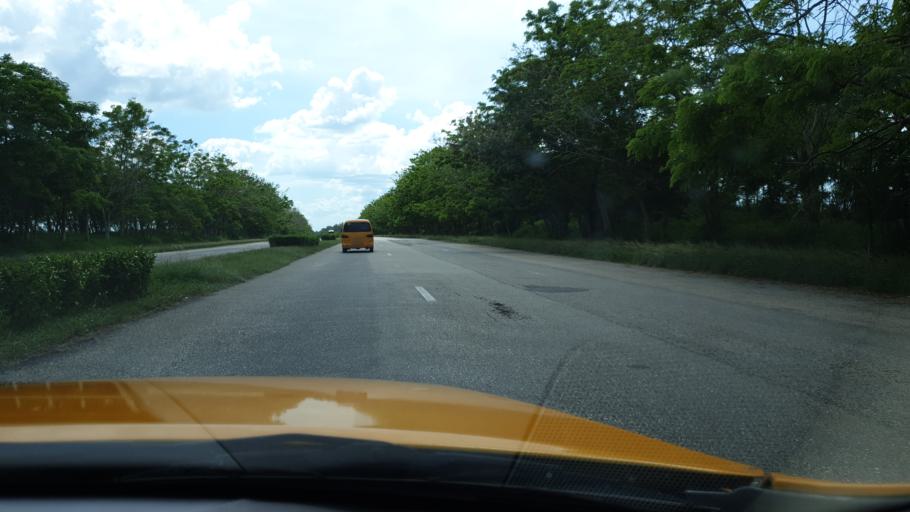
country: CU
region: Cienfuegos
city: Cruces
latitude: 22.4554
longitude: -80.3088
